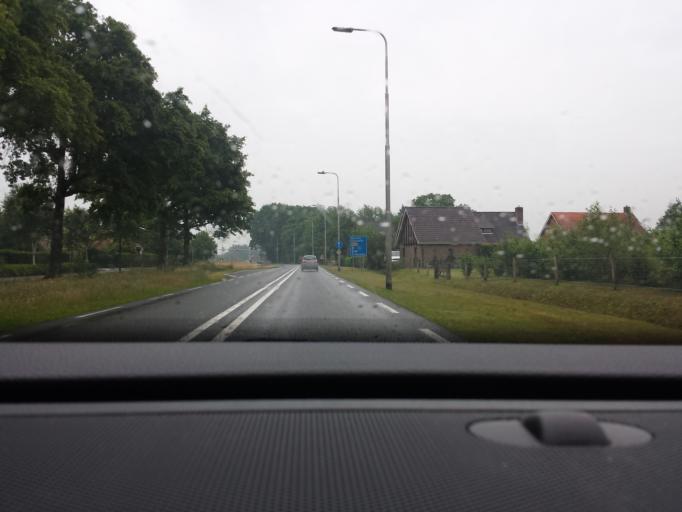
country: NL
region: Overijssel
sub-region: Gemeente Haaksbergen
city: Haaksbergen
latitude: 52.1500
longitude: 6.7396
